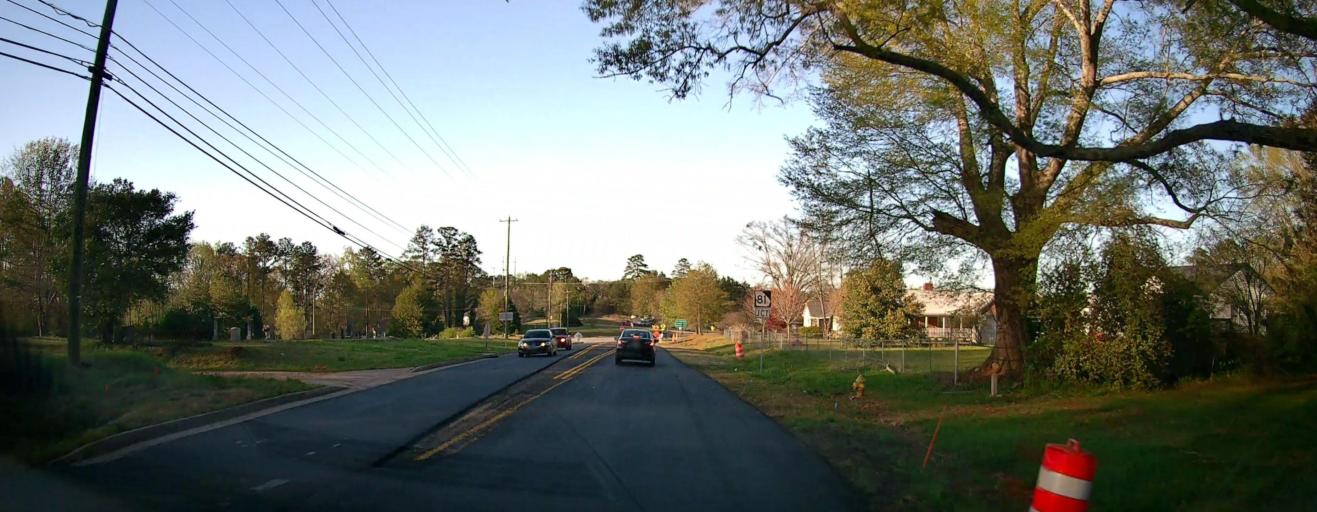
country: US
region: Georgia
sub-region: Newton County
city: Porterdale
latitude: 33.5637
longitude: -83.9043
